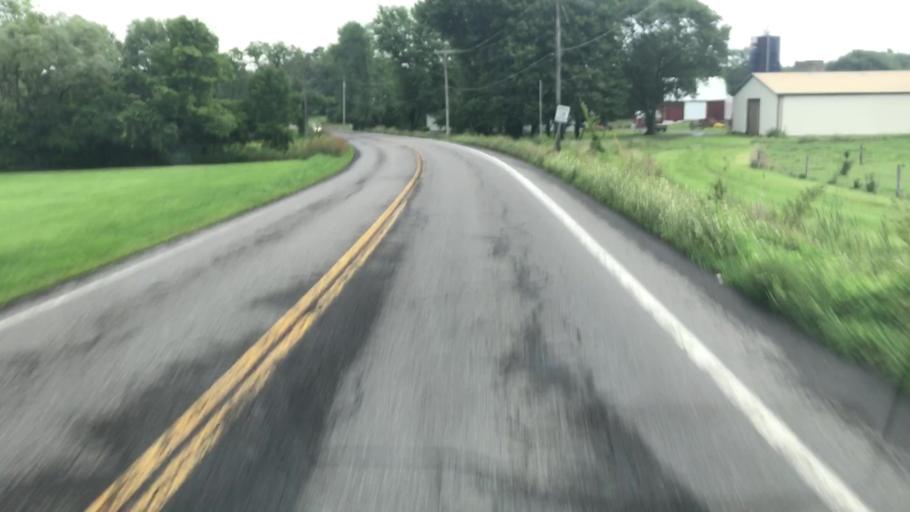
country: US
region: New York
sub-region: Onondaga County
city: Skaneateles
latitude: 42.9588
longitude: -76.4487
